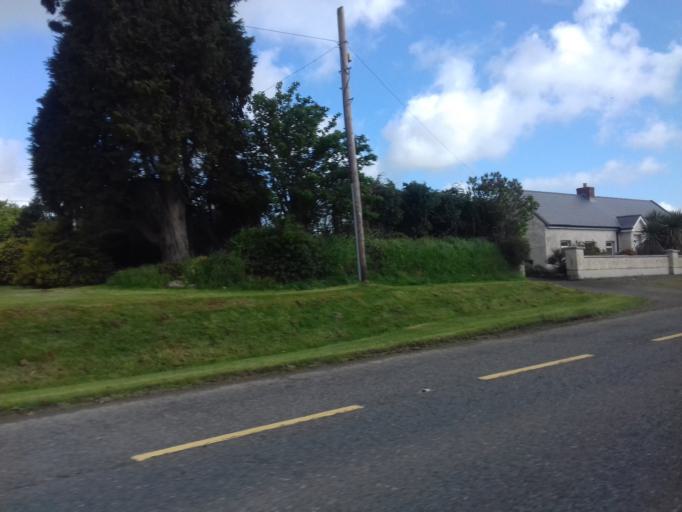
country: IE
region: Leinster
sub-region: Loch Garman
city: Ferns
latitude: 52.6215
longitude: -6.4096
